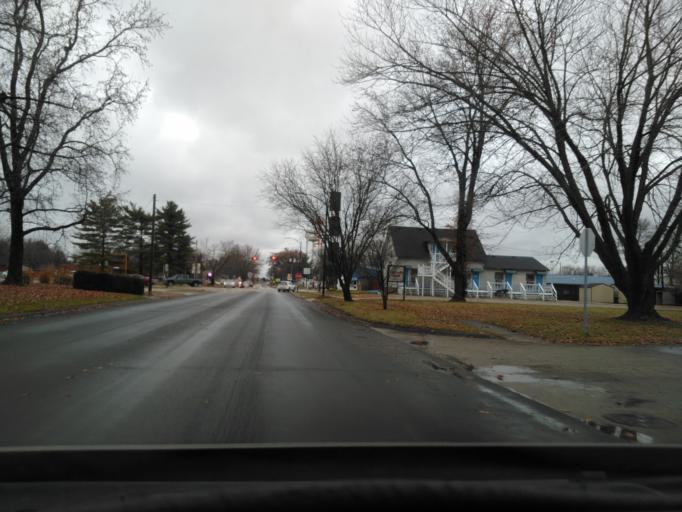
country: US
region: Illinois
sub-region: Effingham County
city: Altamont
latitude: 39.0561
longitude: -88.7480
